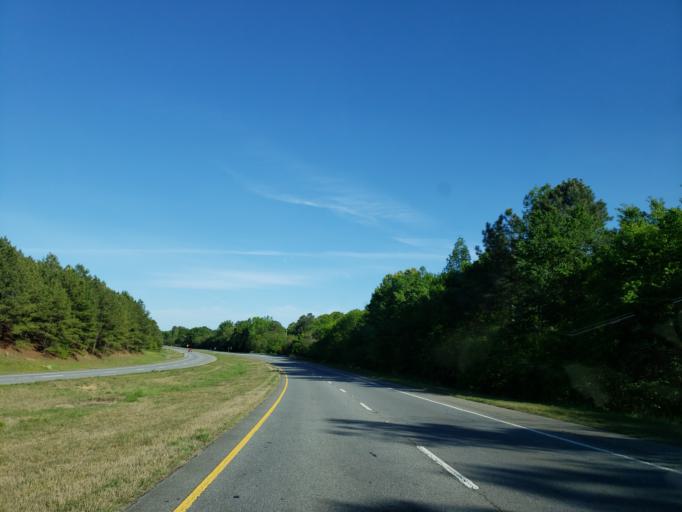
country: US
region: Georgia
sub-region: Polk County
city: Cedartown
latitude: 34.0065
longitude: -85.1754
